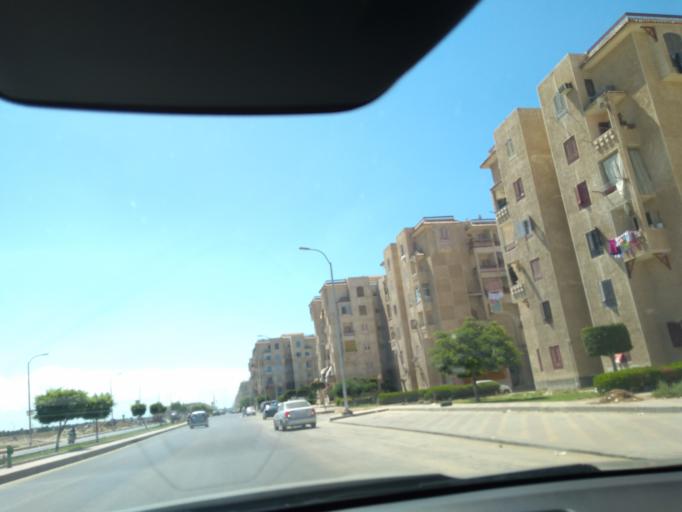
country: EG
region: Dumyat
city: Faraskur
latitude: 31.4242
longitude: 31.6720
